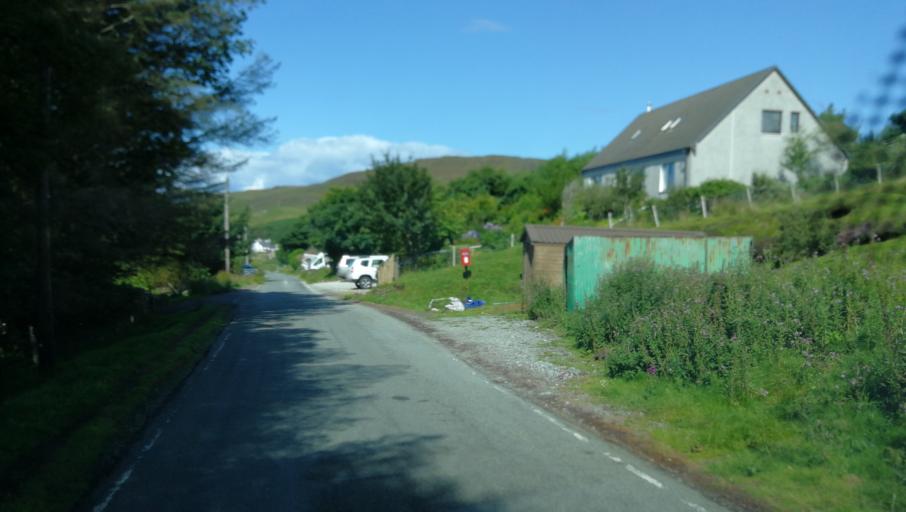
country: GB
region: Scotland
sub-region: Highland
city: Isle of Skye
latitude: 57.4486
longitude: -6.6913
